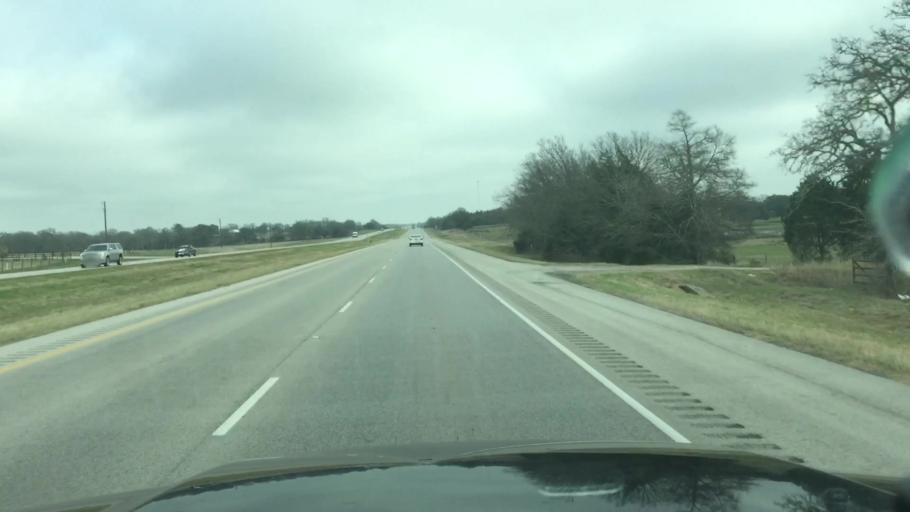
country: US
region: Texas
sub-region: Lee County
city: Giddings
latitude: 30.1452
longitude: -96.7226
